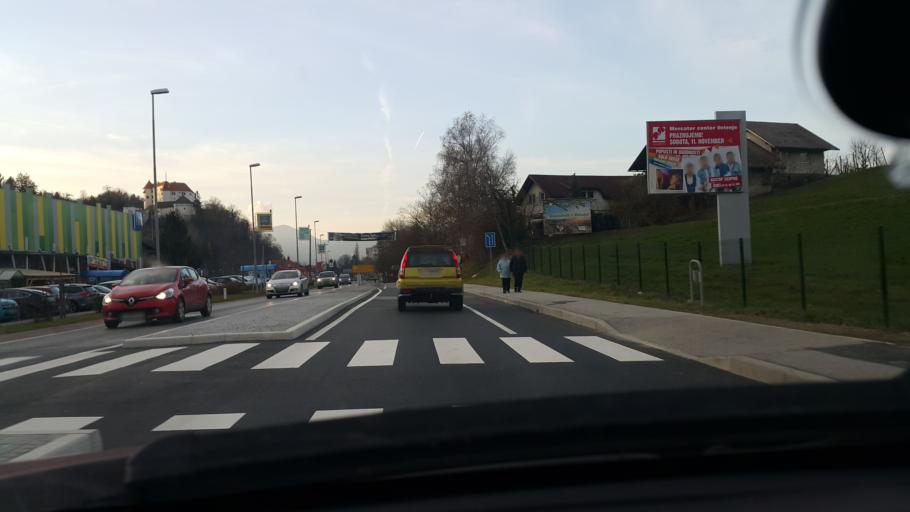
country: SI
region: Velenje
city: Velenje
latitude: 46.3554
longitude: 15.1176
